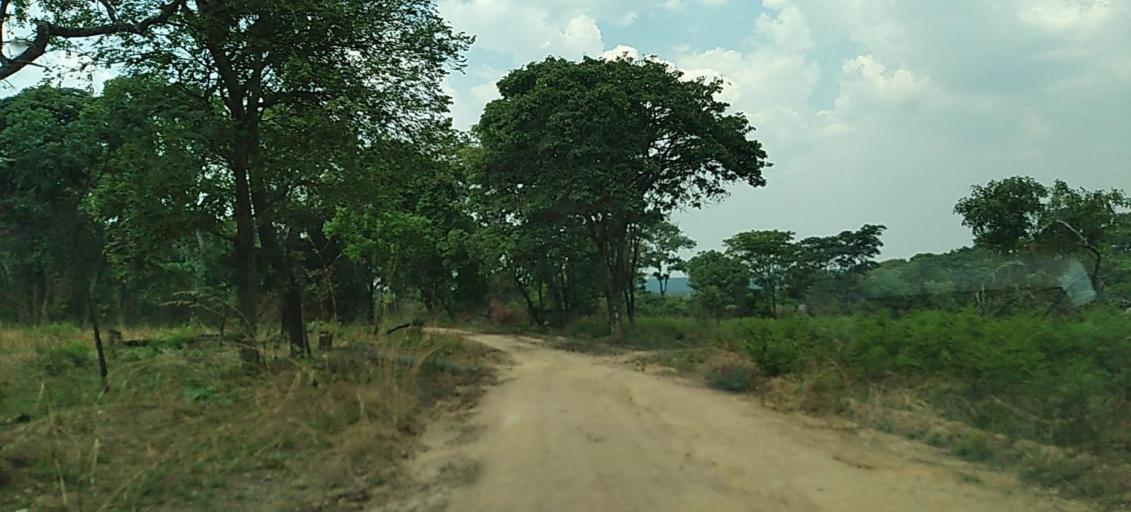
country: ZM
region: Copperbelt
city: Chingola
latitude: -12.7532
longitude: 27.7231
